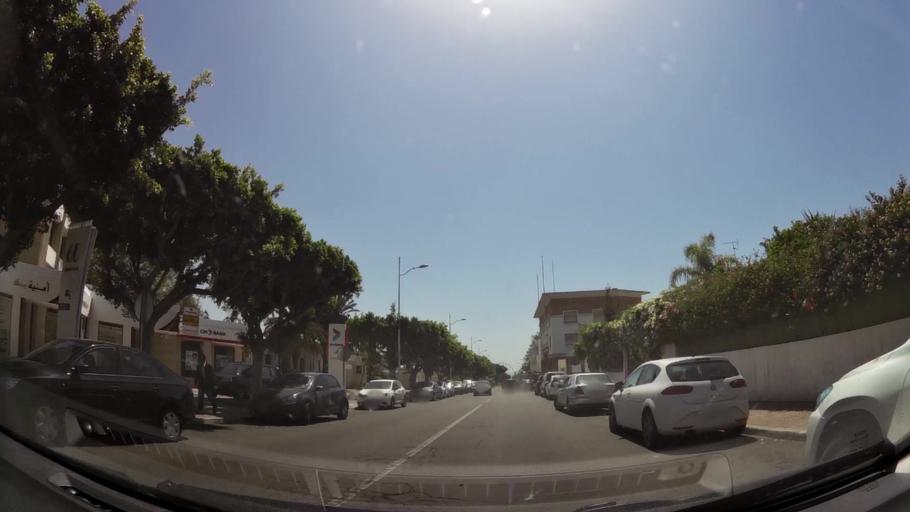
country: MA
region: Souss-Massa-Draa
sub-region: Agadir-Ida-ou-Tnan
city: Agadir
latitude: 30.4243
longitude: -9.6022
